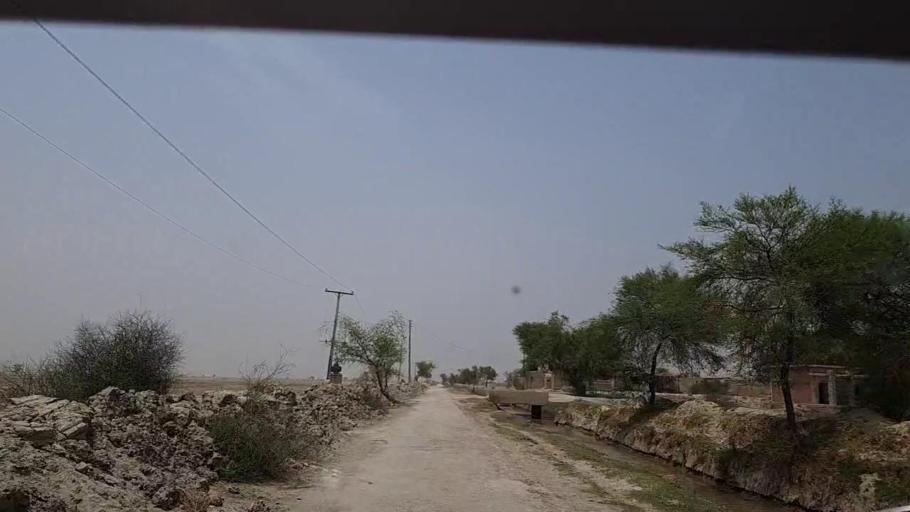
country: PK
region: Sindh
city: Khairpur Nathan Shah
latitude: 27.0461
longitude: 67.6189
